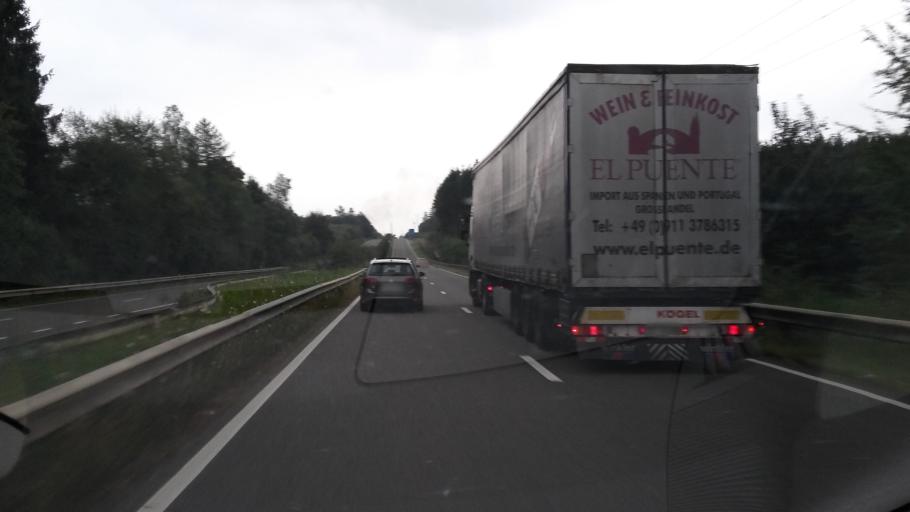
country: BE
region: Wallonia
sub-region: Province du Luxembourg
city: Bertrix
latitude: 49.8970
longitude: 5.3124
